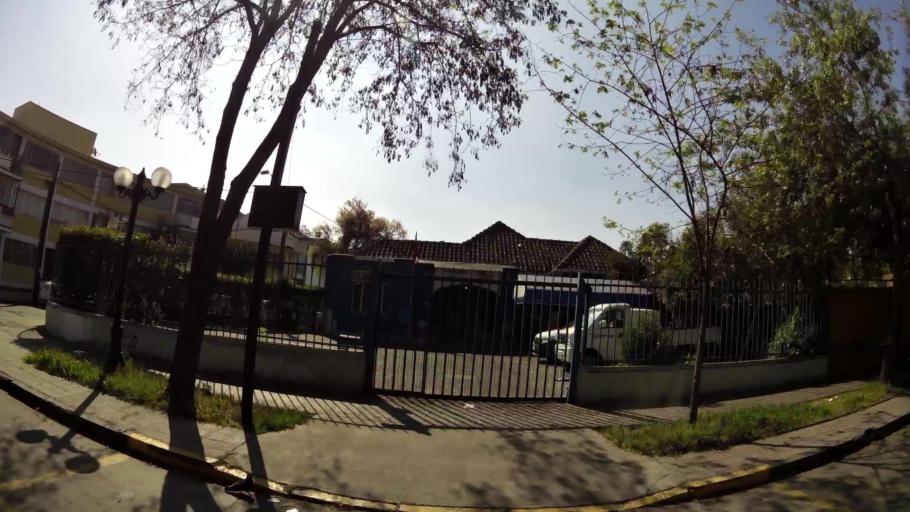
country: CL
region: Santiago Metropolitan
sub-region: Provincia de Santiago
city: Santiago
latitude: -33.4493
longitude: -70.6287
